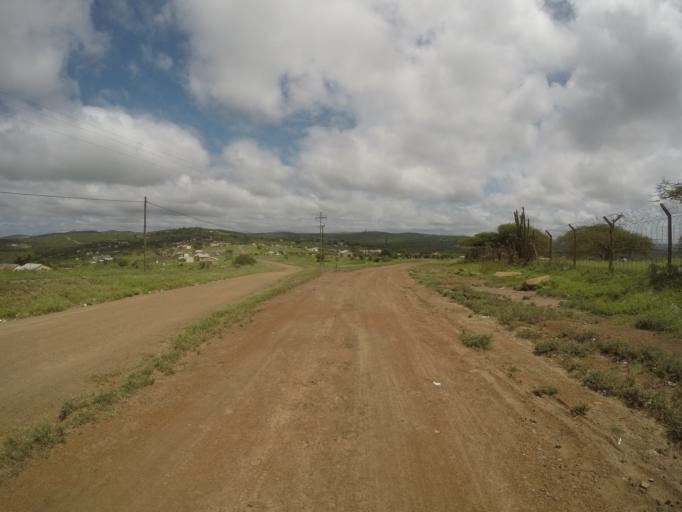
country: ZA
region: KwaZulu-Natal
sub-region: uThungulu District Municipality
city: Empangeni
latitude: -28.5767
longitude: 31.8418
